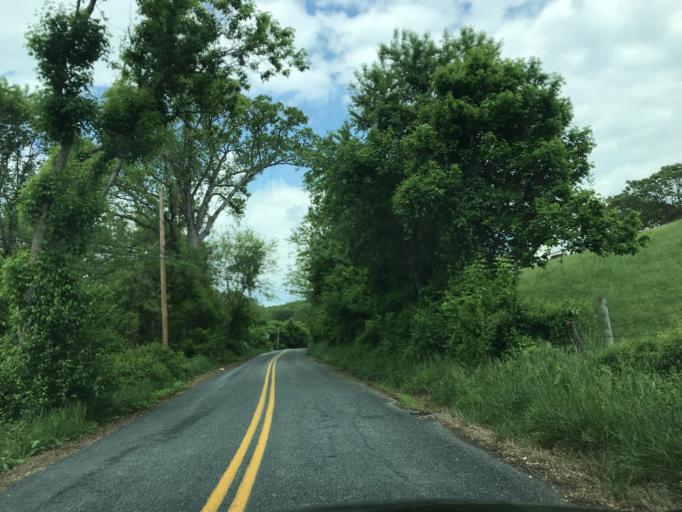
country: US
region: Maryland
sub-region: Harford County
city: Bel Air North
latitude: 39.6190
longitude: -76.3342
